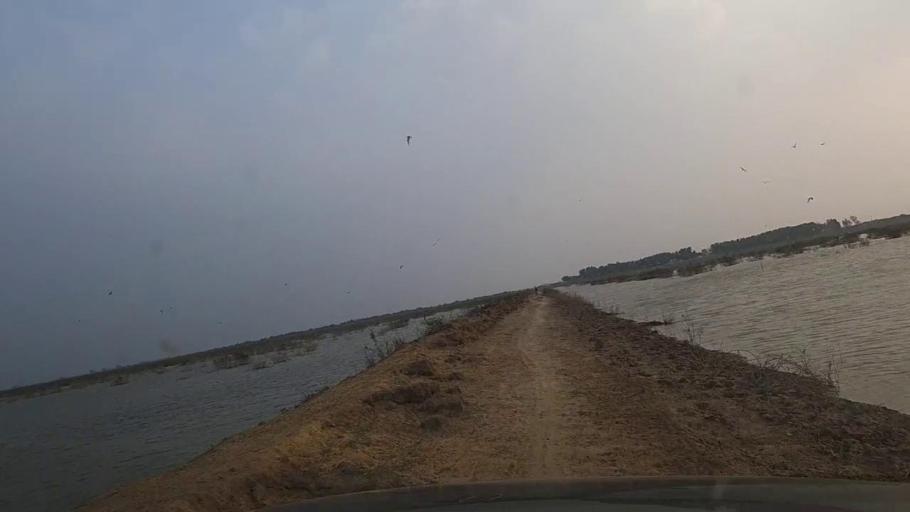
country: PK
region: Sindh
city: Gharo
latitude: 24.7683
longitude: 67.6918
